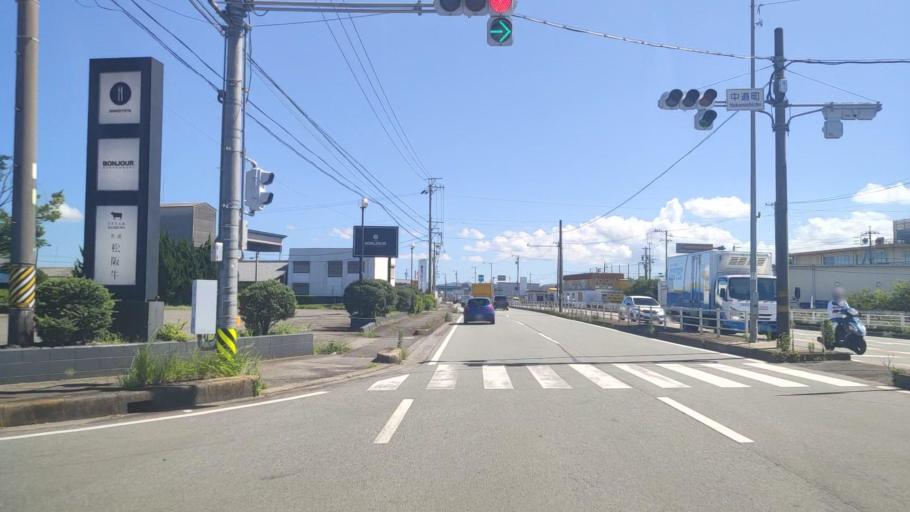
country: JP
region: Mie
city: Hisai-motomachi
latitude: 34.6209
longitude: 136.5156
